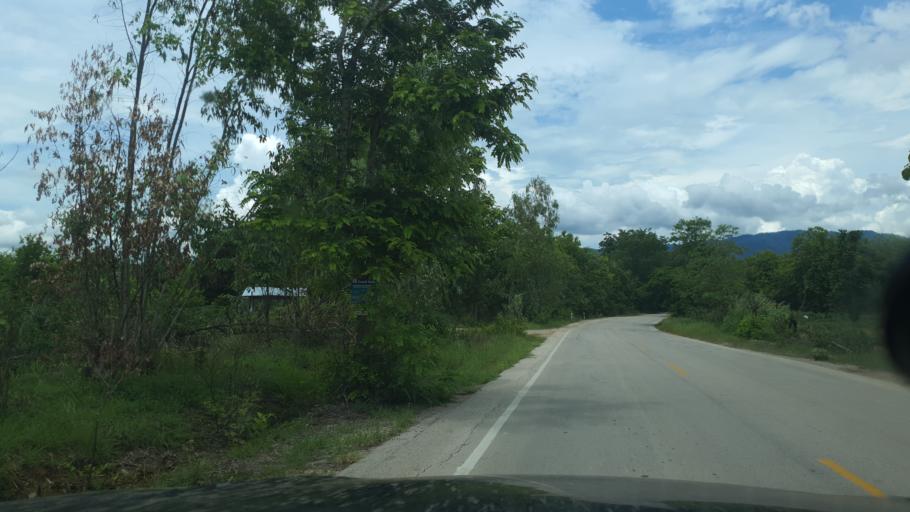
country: TH
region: Lampang
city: Sop Prap
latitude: 17.9267
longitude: 99.3776
